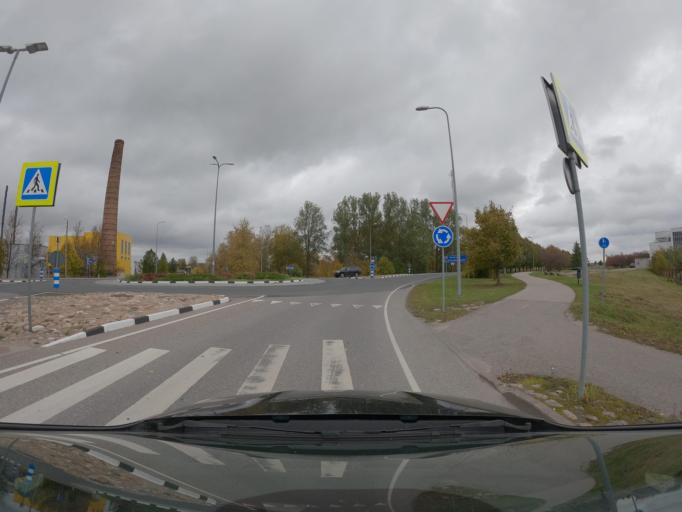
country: EE
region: Saare
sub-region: Kuressaare linn
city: Kuressaare
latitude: 58.2677
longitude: 22.4900
